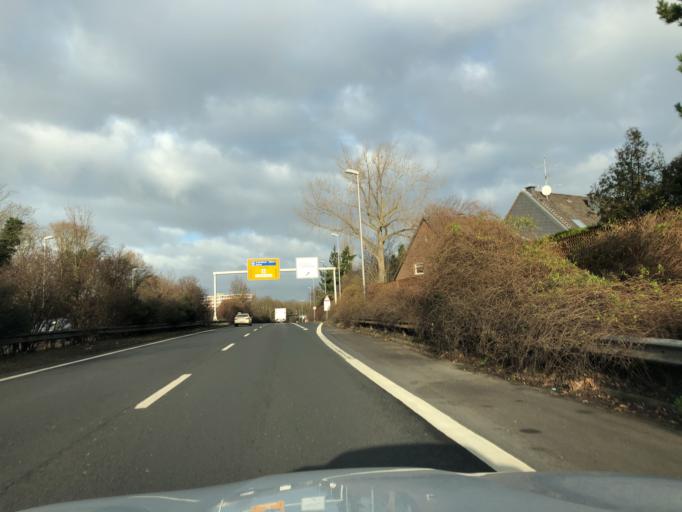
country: DE
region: North Rhine-Westphalia
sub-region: Regierungsbezirk Dusseldorf
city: Dusseldorf
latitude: 51.2640
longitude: 6.7581
